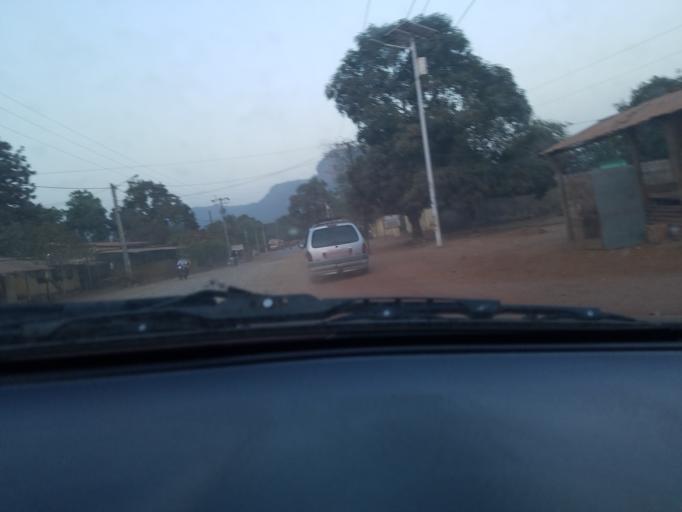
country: GN
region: Kindia
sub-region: Prefecture de Dubreka
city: Dubreka
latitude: 9.7893
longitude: -13.4944
